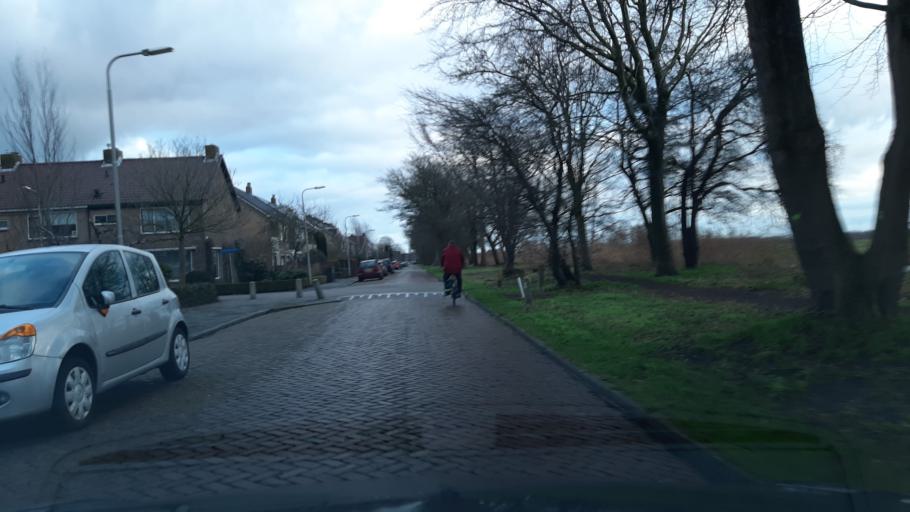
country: NL
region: South Holland
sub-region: Gemeente Hillegom
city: Hillegom
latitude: 52.2820
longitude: 4.5756
